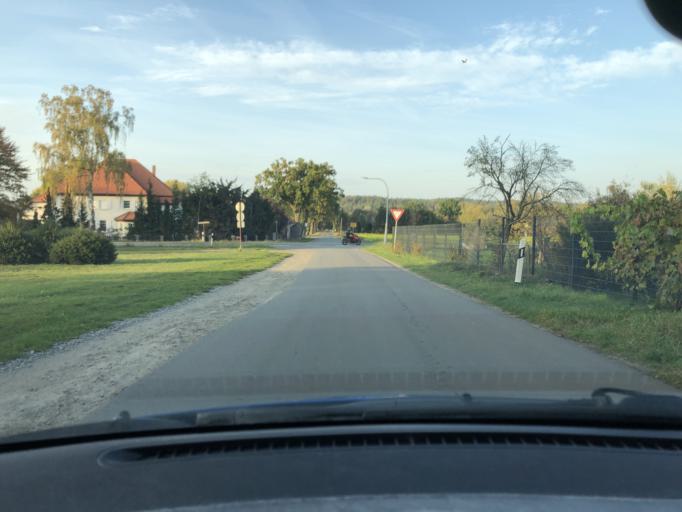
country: DE
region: Lower Saxony
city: Hitzacker
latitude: 53.1456
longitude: 11.0039
